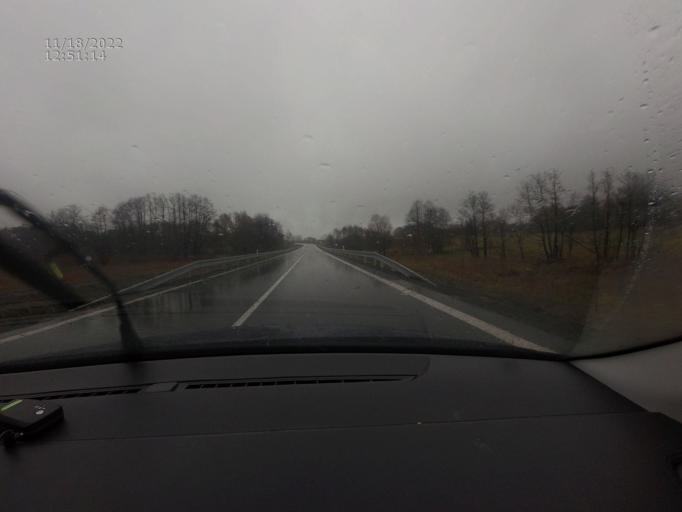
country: CZ
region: Plzensky
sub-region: Okres Klatovy
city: Kolinec
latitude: 49.3300
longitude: 13.4371
